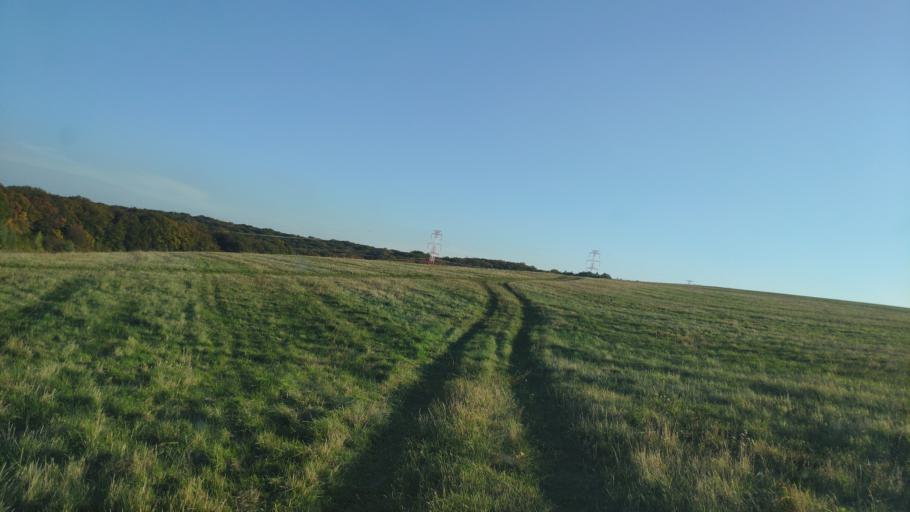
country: SK
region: Kosicky
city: Kosice
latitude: 48.7156
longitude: 21.1680
